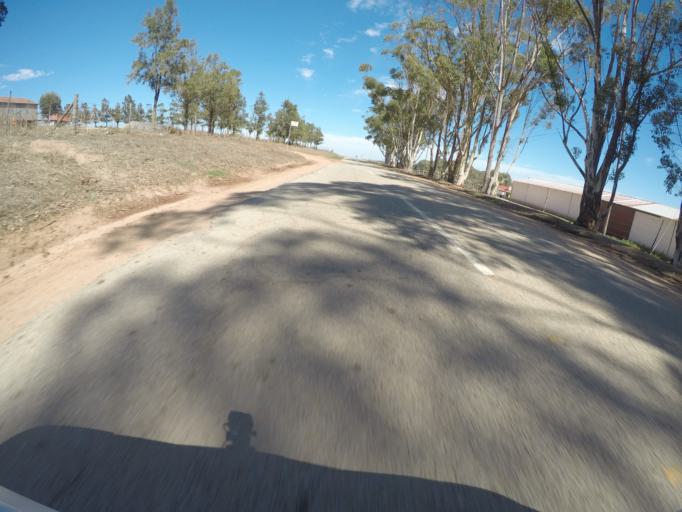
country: ZA
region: Western Cape
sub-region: City of Cape Town
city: Atlantis
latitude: -33.6125
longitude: 18.6365
